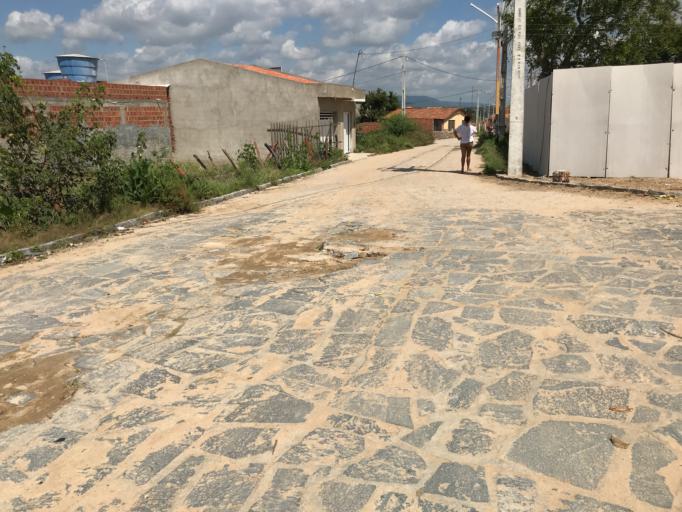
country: BR
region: Pernambuco
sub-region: Bezerros
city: Bezerros
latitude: -8.2276
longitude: -35.7566
